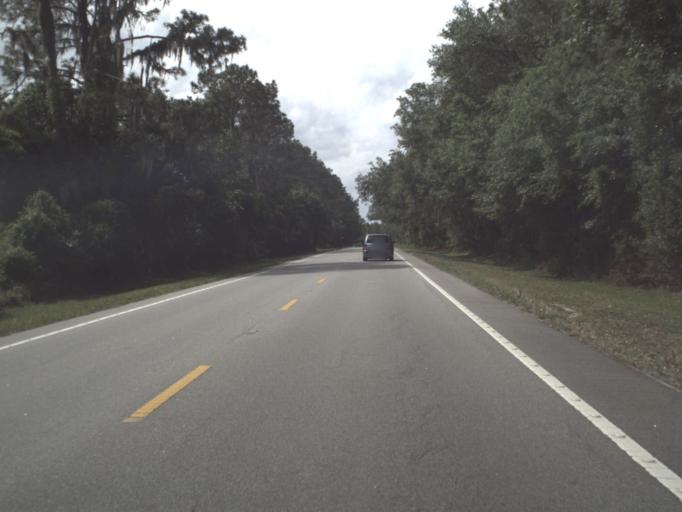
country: US
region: Florida
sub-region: Putnam County
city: Crescent City
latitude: 29.5079
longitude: -81.4937
